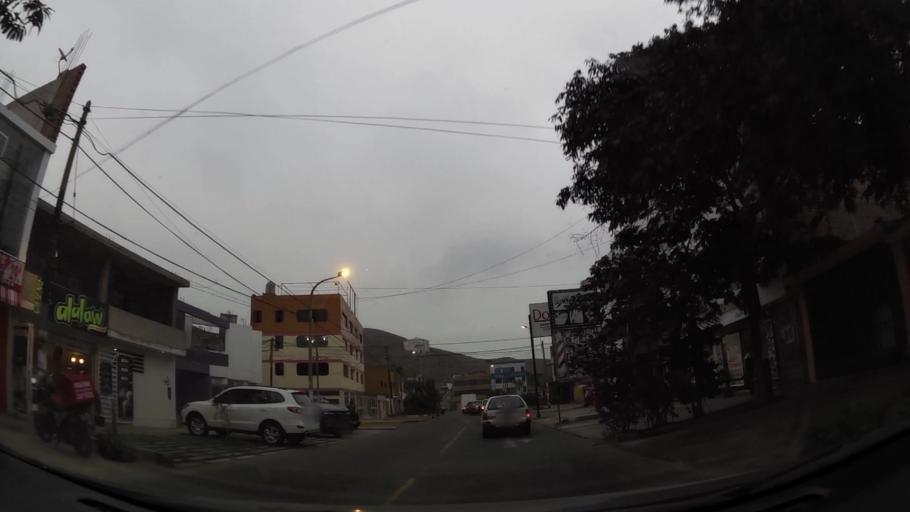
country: PE
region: Lima
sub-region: Lima
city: Independencia
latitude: -11.9373
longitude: -77.0783
